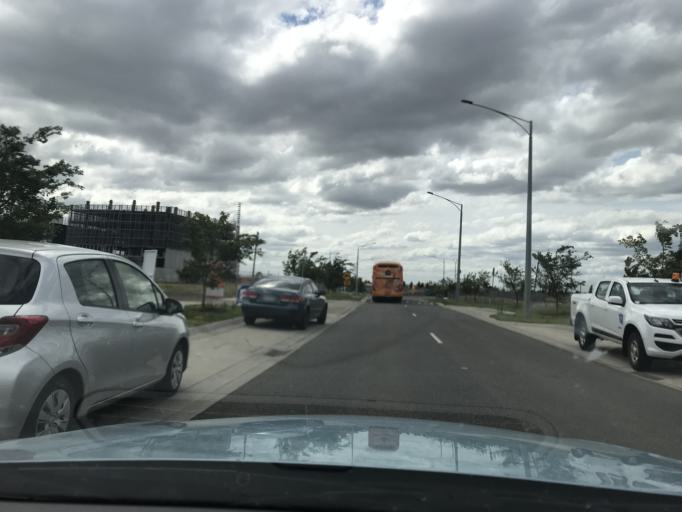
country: AU
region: Victoria
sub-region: Wyndham
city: Williams Landing
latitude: -37.8684
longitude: 144.7459
